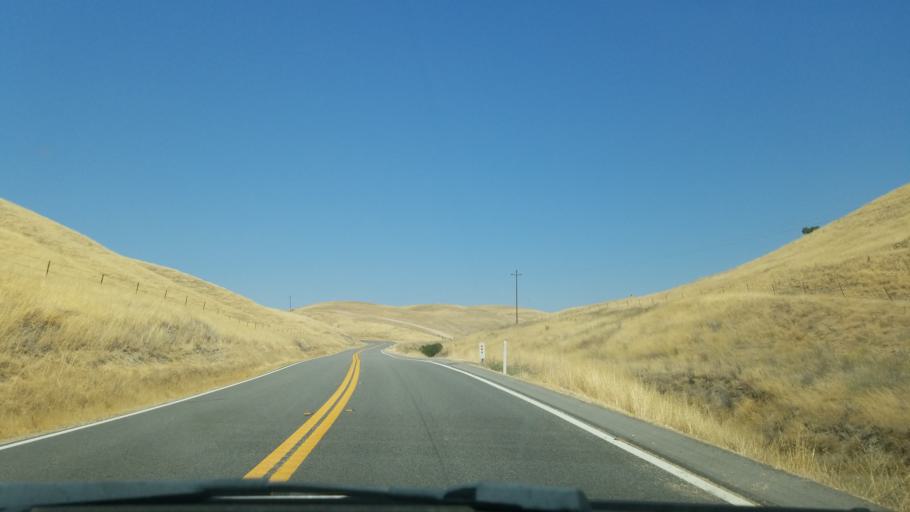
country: US
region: California
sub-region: San Luis Obispo County
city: Shandon
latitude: 35.5891
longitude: -120.4237
